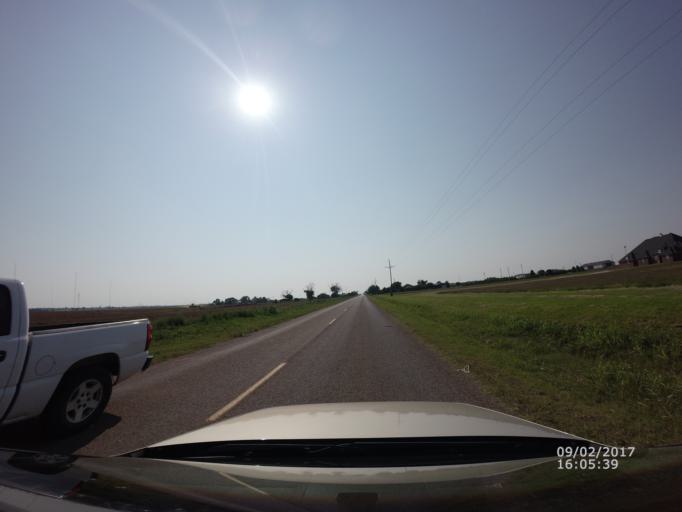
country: US
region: New Mexico
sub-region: Curry County
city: Clovis
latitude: 34.4484
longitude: -103.2033
